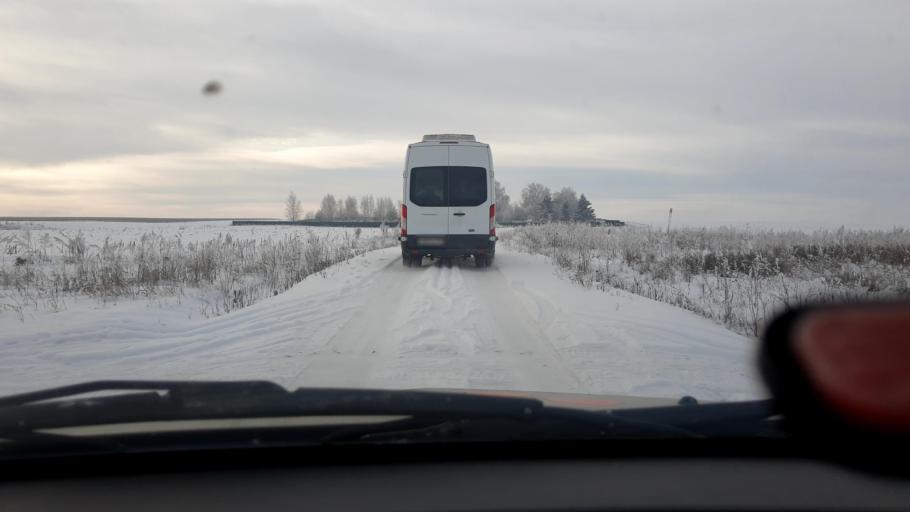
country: RU
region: Bashkortostan
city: Tolbazy
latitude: 54.3545
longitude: 55.8421
